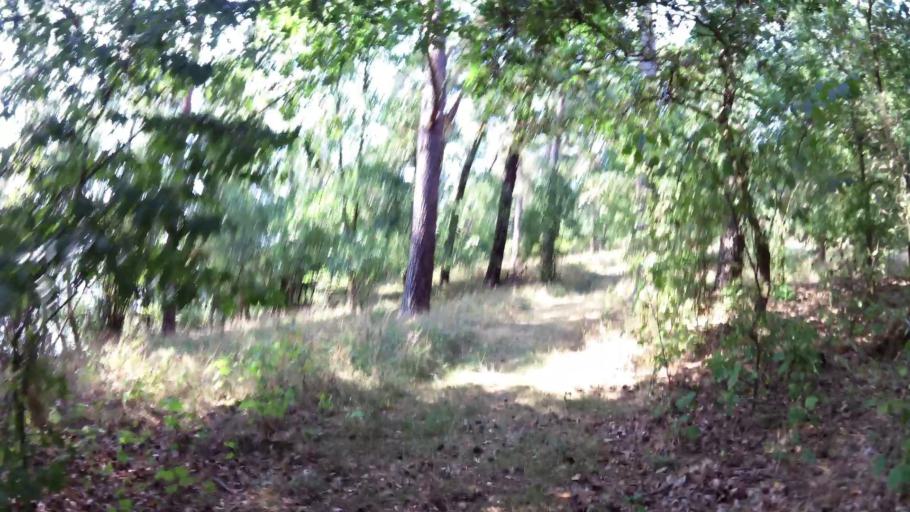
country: PL
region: West Pomeranian Voivodeship
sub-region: Powiat gryfinski
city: Moryn
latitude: 52.8695
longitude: 14.4171
